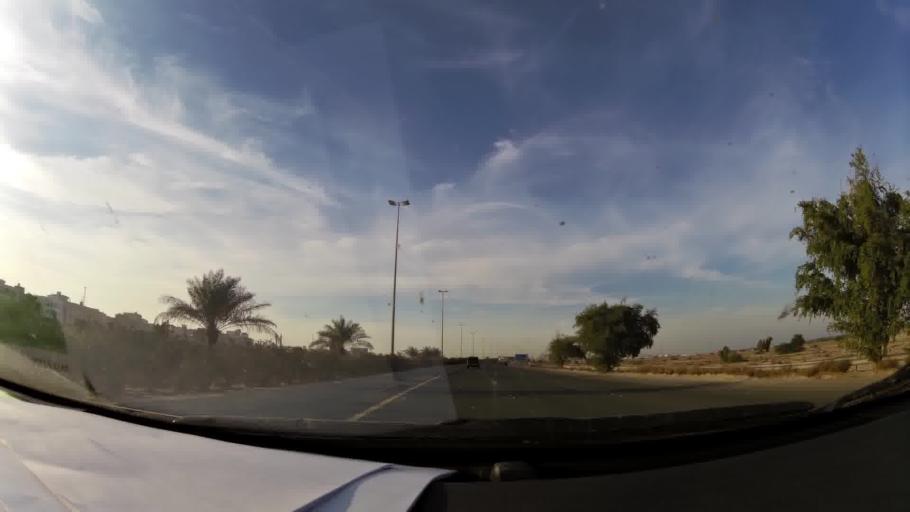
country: KW
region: Al Ahmadi
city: Al Fahahil
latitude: 28.9600
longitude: 48.1680
